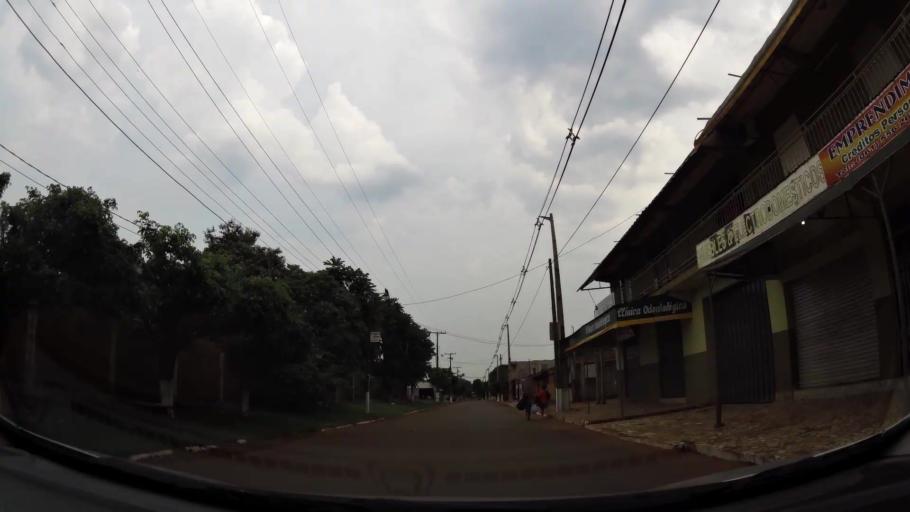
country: PY
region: Alto Parana
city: Presidente Franco
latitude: -25.5516
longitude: -54.6417
